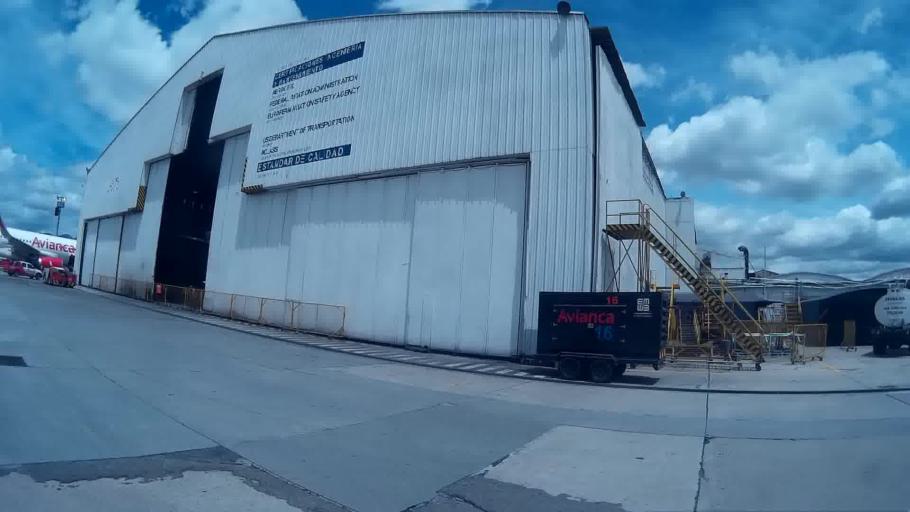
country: CO
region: Cundinamarca
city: Funza
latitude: 4.6956
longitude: -74.1345
